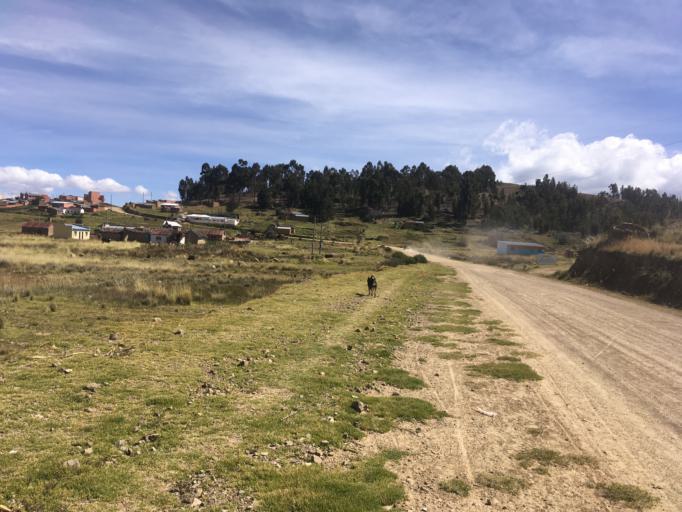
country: BO
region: La Paz
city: San Pedro
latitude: -16.2610
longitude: -68.8764
